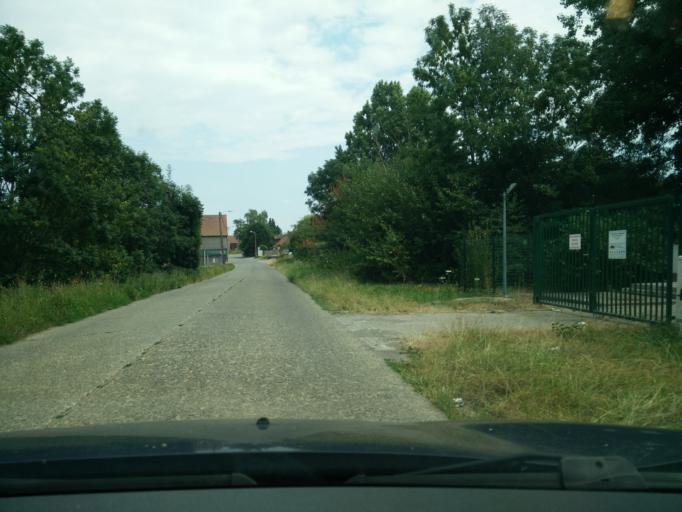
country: BE
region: Wallonia
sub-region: Province du Hainaut
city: Ecaussinnes-d'Enghien
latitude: 50.5544
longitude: 4.1267
